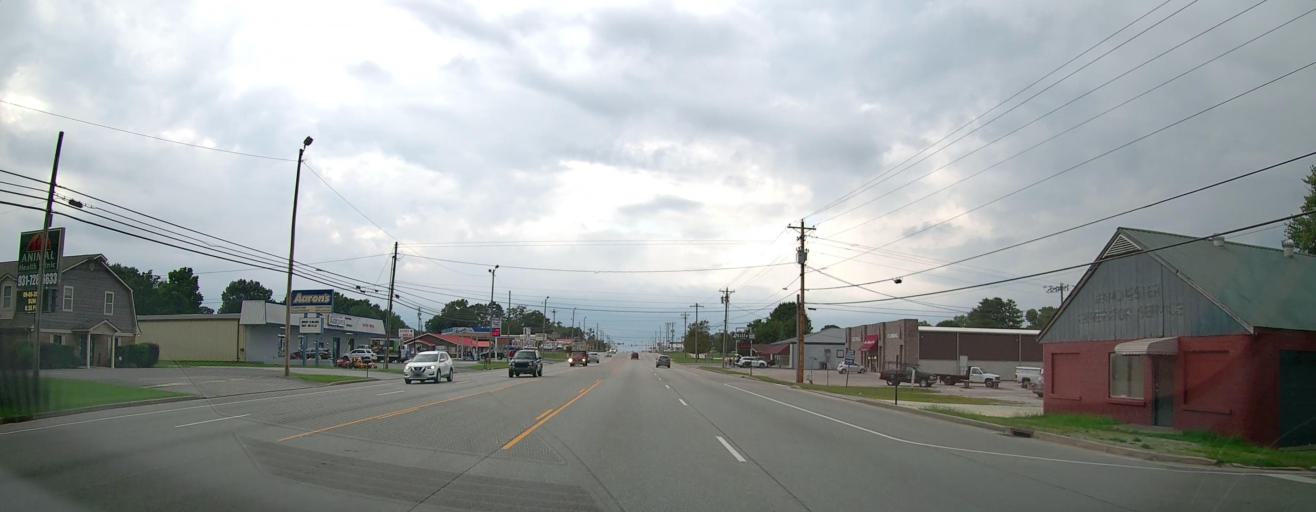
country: US
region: Tennessee
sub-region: Coffee County
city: Manchester
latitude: 35.4656
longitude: -86.0688
